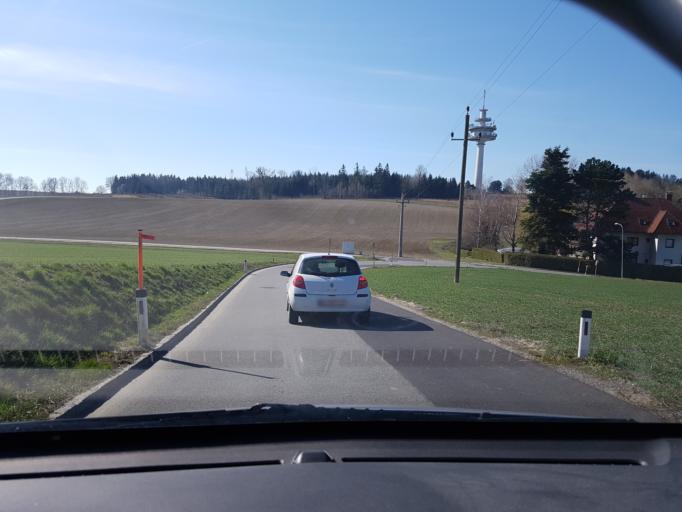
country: AT
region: Upper Austria
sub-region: Politischer Bezirk Linz-Land
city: Ansfelden
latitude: 48.2065
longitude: 14.2964
